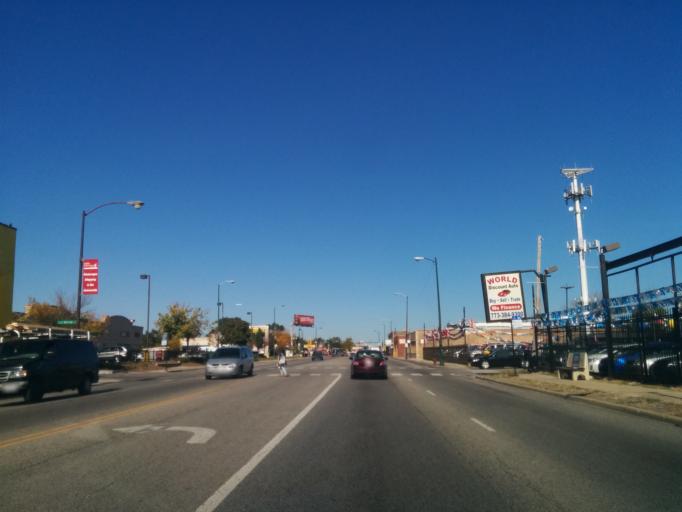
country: US
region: Illinois
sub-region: Cook County
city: Oak Park
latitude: 41.9073
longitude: -87.7460
